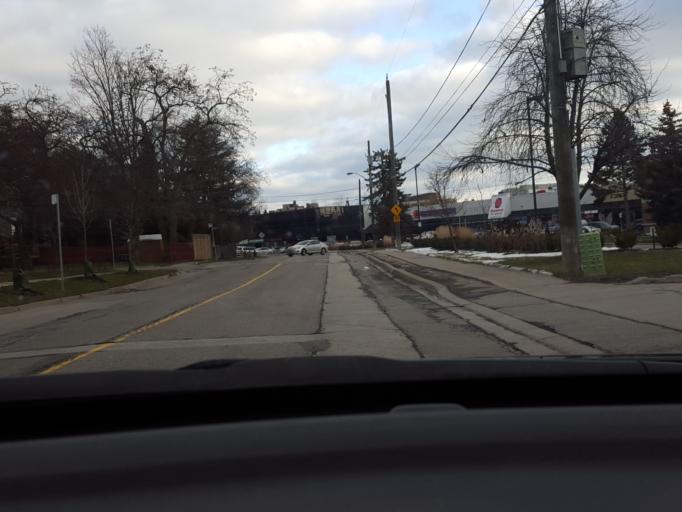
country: CA
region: Ontario
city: Willowdale
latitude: 43.7279
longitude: -79.3441
